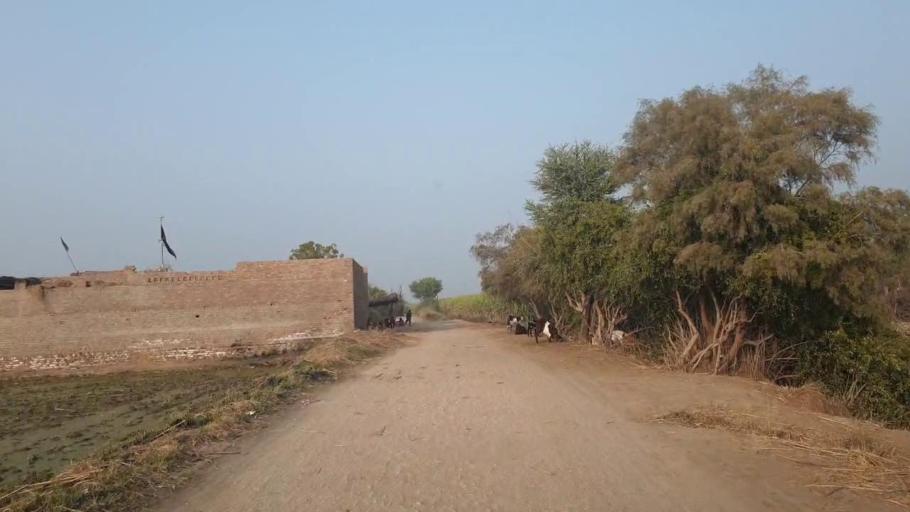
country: PK
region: Sindh
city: Shahdadpur
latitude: 25.8749
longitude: 68.6033
